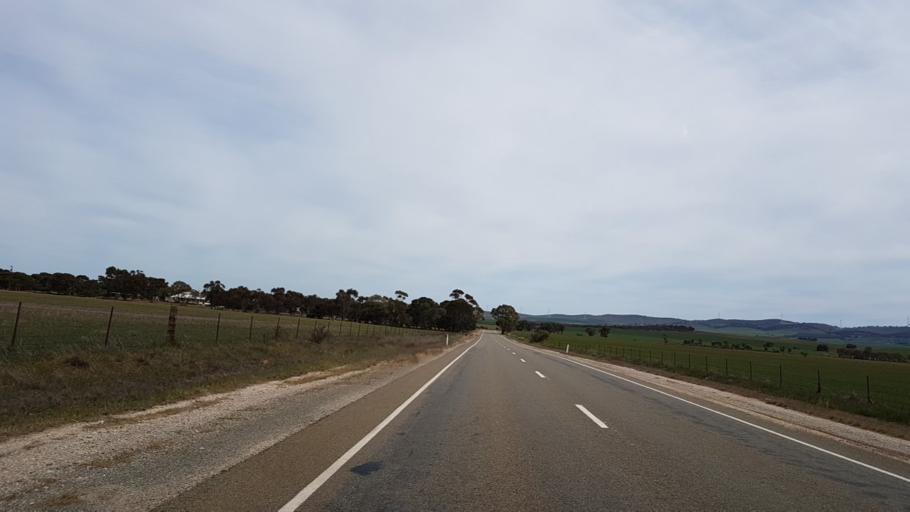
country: AU
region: South Australia
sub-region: Peterborough
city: Peterborough
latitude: -33.0277
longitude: 138.6679
